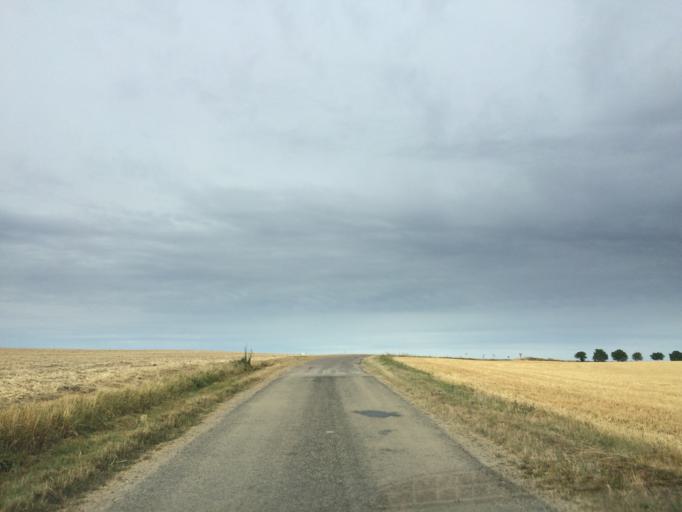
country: FR
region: Bourgogne
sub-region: Departement de l'Yonne
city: Aillant-sur-Tholon
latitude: 47.8576
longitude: 3.3767
